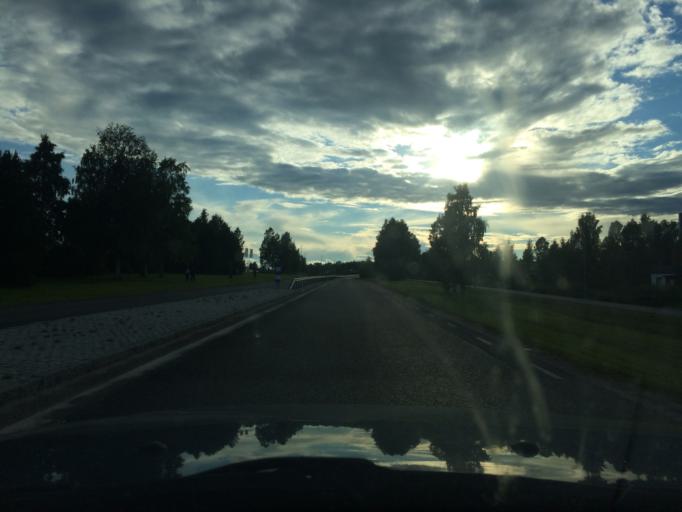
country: SE
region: Norrbotten
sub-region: Pitea Kommun
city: Pitea
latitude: 65.3241
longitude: 21.4478
